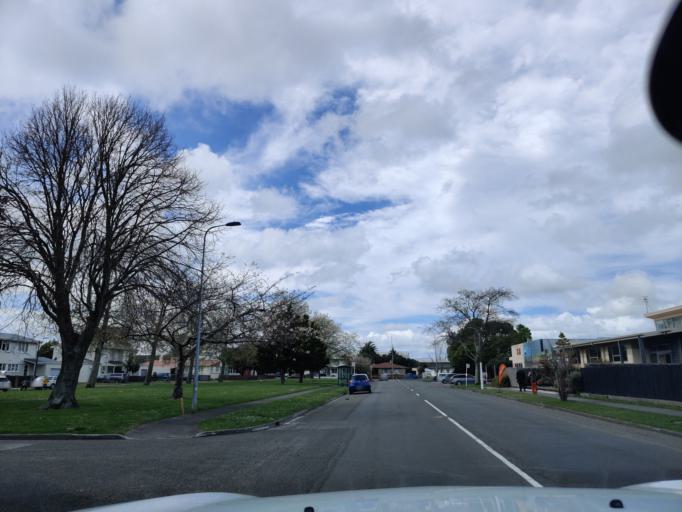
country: NZ
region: Manawatu-Wanganui
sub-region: Palmerston North City
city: Palmerston North
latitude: -40.3600
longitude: 175.5850
